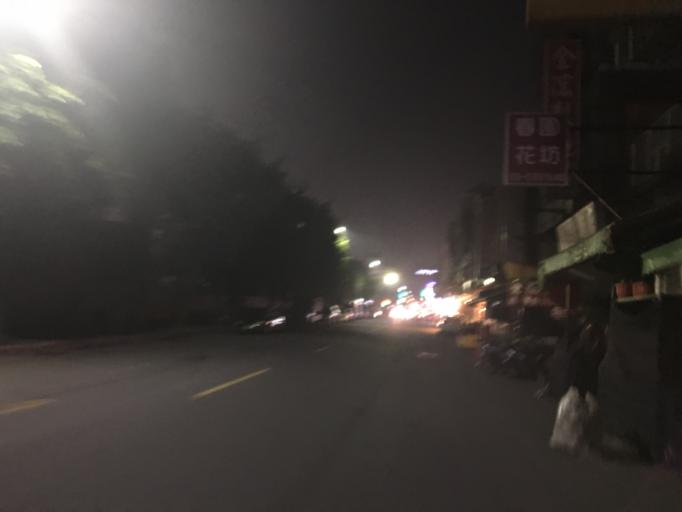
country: TW
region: Taiwan
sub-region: Hsinchu
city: Hsinchu
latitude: 24.8121
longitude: 120.9786
